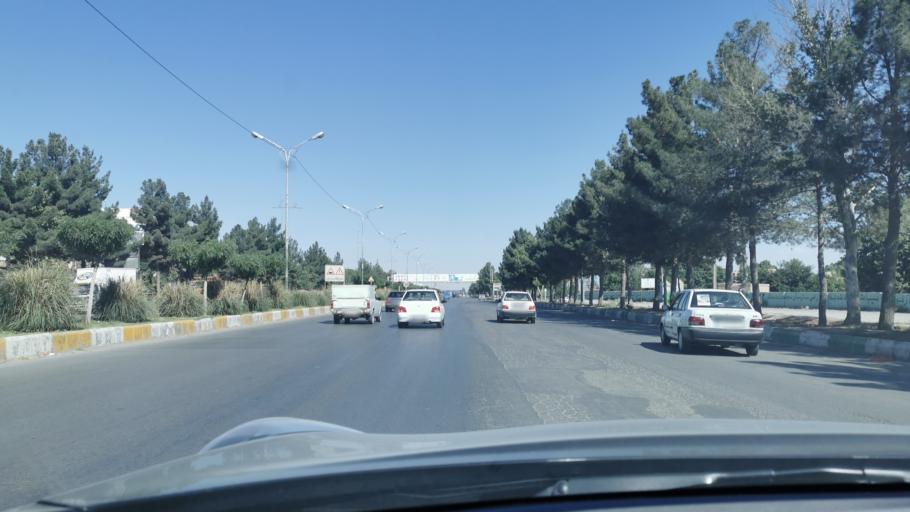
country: IR
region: Razavi Khorasan
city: Chenaran
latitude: 36.6366
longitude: 59.1259
